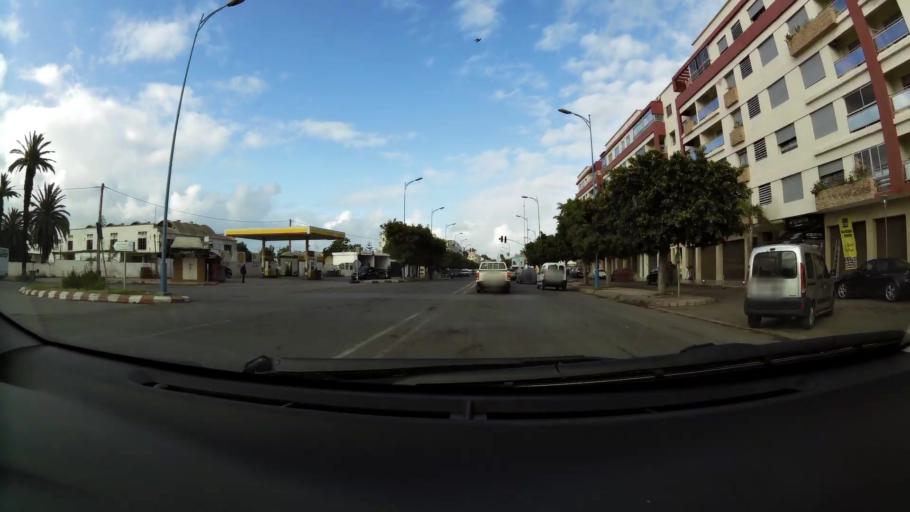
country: MA
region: Grand Casablanca
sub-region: Mohammedia
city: Mohammedia
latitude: 33.6918
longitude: -7.3939
